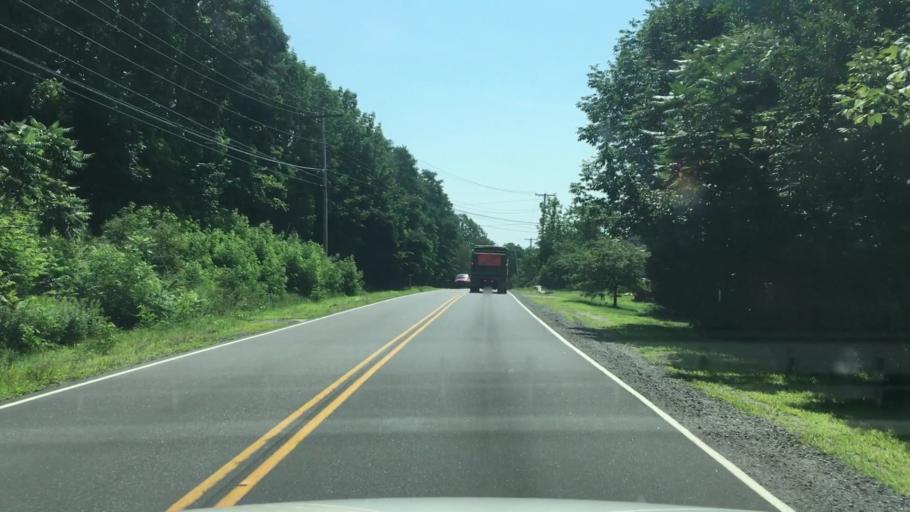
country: US
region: Maine
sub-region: Kennebec County
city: Hallowell
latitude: 44.3049
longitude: -69.8208
